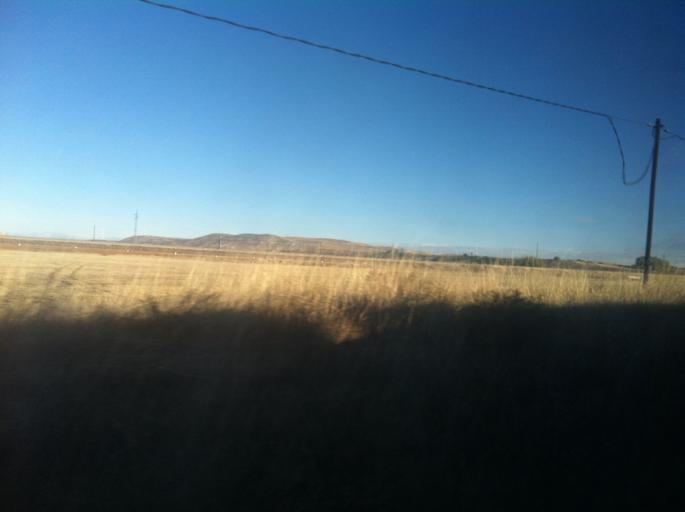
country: ES
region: Castille and Leon
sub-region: Provincia de Palencia
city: Villodrigo
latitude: 42.1359
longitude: -4.1258
